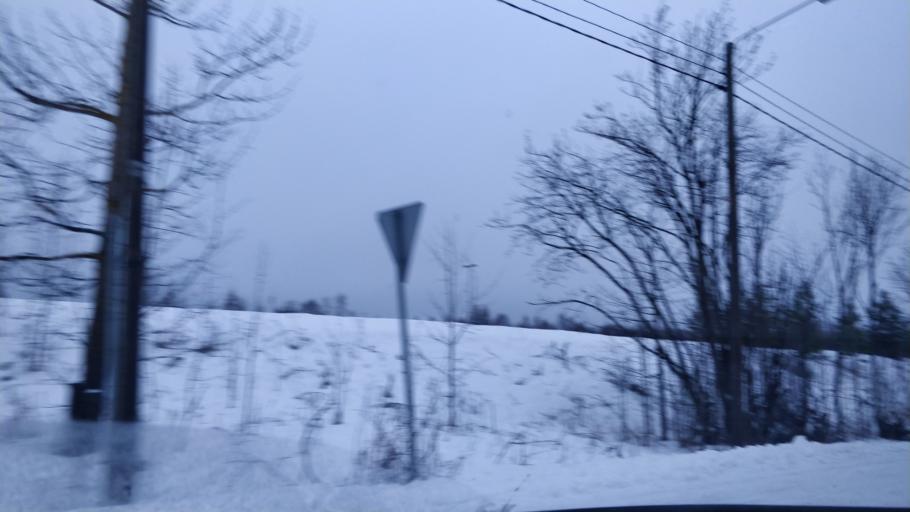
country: FI
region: Lapland
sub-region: Kemi-Tornio
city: Kemi
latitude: 65.7462
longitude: 24.5784
